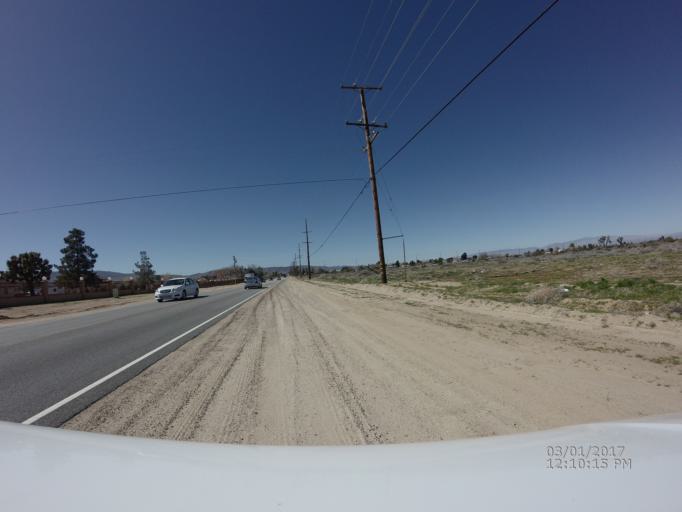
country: US
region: California
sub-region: Los Angeles County
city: Desert View Highlands
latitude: 34.6312
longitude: -118.1608
